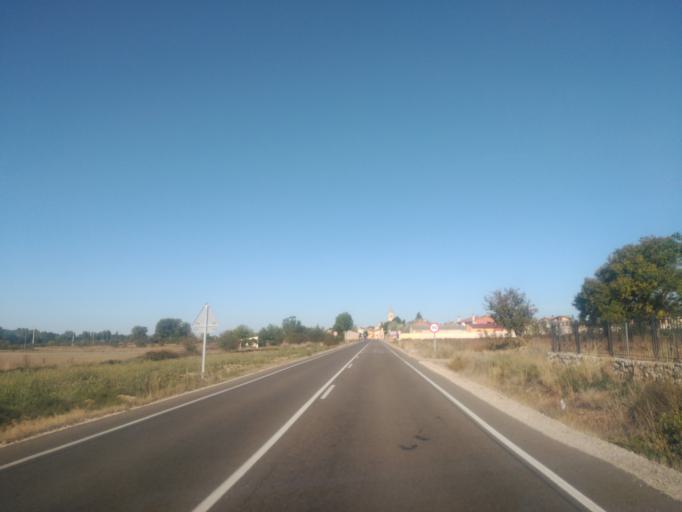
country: ES
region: Castille and Leon
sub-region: Provincia de Burgos
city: Zazuar
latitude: 41.6939
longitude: -3.5472
